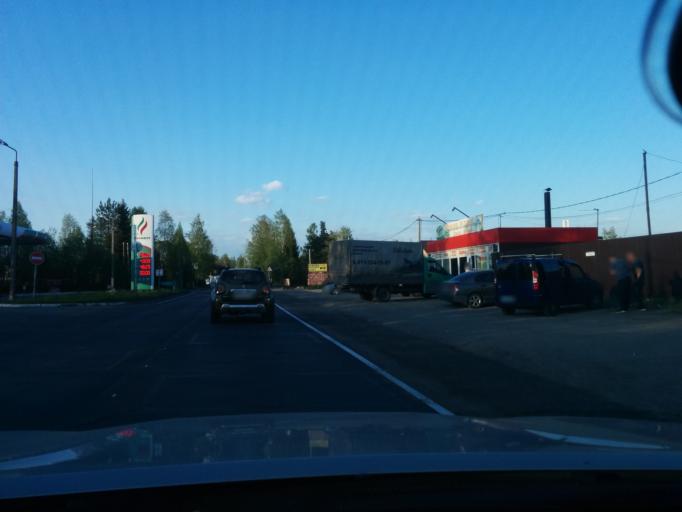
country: RU
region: Leningrad
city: Luppolovo
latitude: 60.1779
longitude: 30.3625
